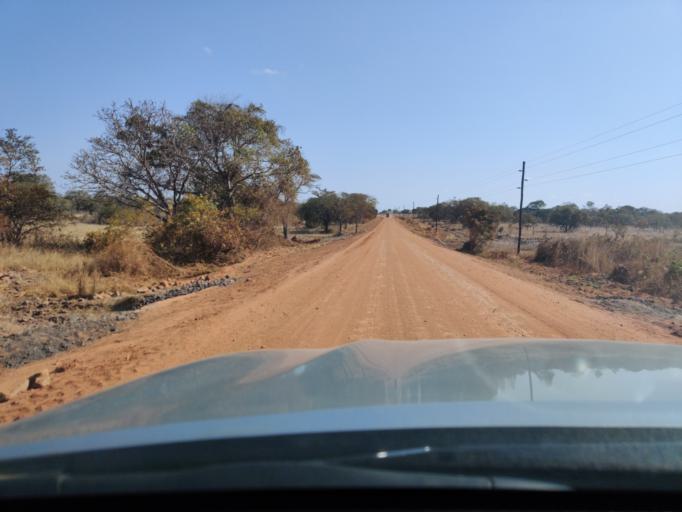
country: ZM
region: Central
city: Mkushi
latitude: -13.9900
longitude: 29.5339
